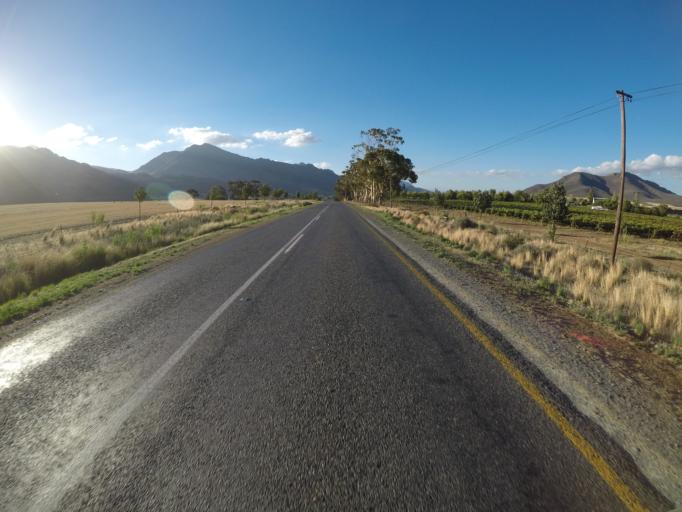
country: ZA
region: Western Cape
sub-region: Cape Winelands District Municipality
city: Worcester
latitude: -33.8898
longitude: 19.3654
